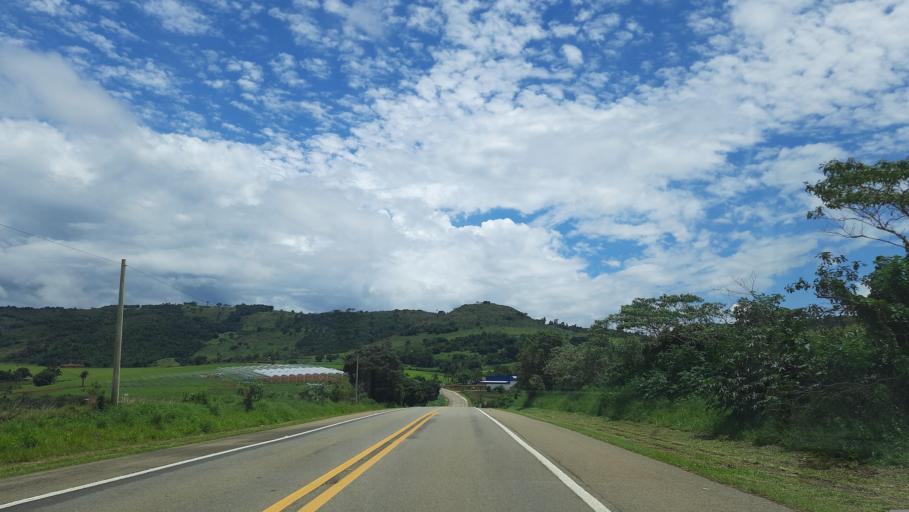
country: BR
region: Sao Paulo
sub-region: Vargem Grande Do Sul
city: Vargem Grande do Sul
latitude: -21.8173
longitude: -46.7845
